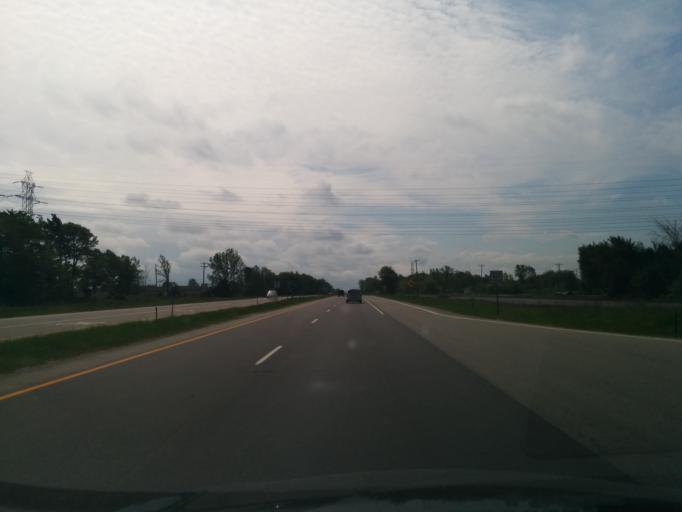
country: US
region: Michigan
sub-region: Ottawa County
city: Beechwood
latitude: 42.9119
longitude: -86.1422
